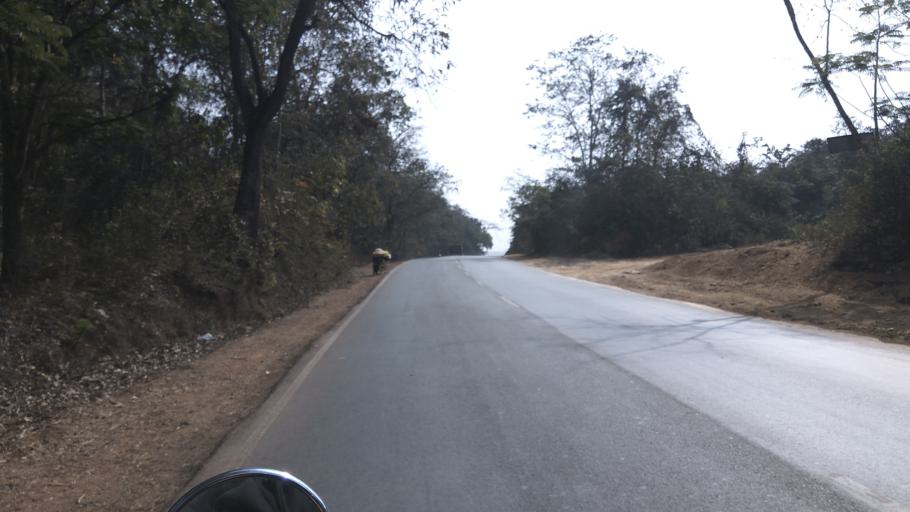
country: IN
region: Goa
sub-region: North Goa
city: Palle
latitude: 15.3970
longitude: 74.1093
